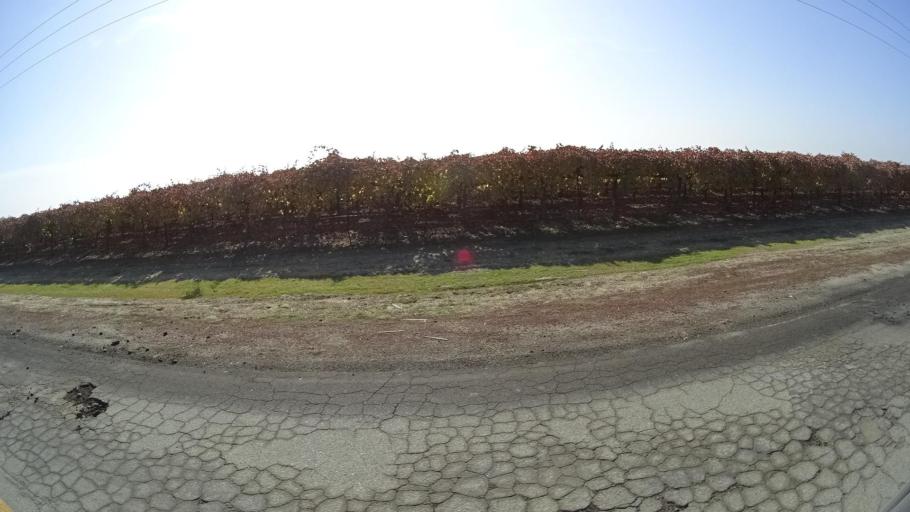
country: US
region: California
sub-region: Kern County
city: McFarland
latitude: 35.6891
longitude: -119.1653
